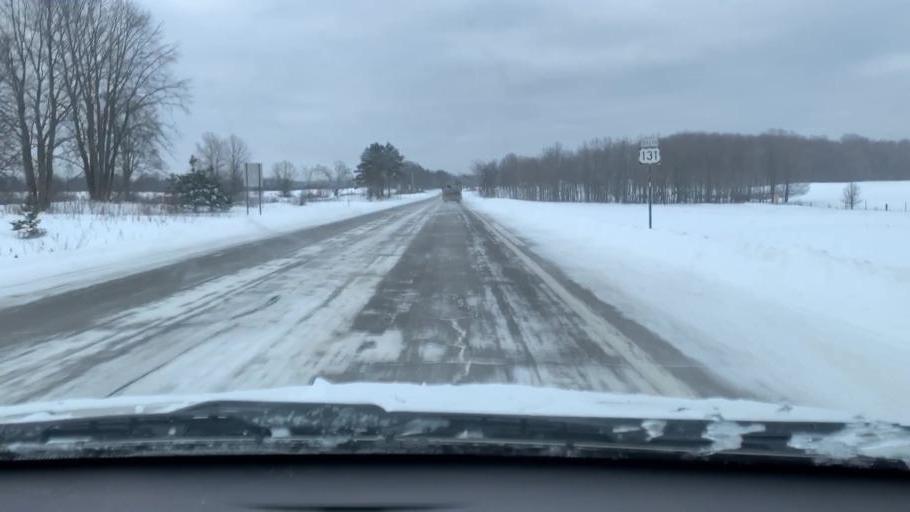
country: US
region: Michigan
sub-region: Wexford County
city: Manton
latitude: 44.5980
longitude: -85.3308
